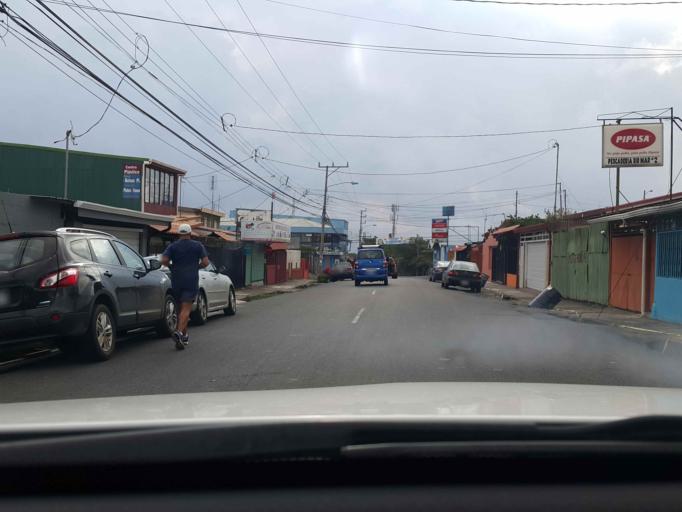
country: CR
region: Heredia
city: San Josecito
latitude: 10.0161
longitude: -84.0992
